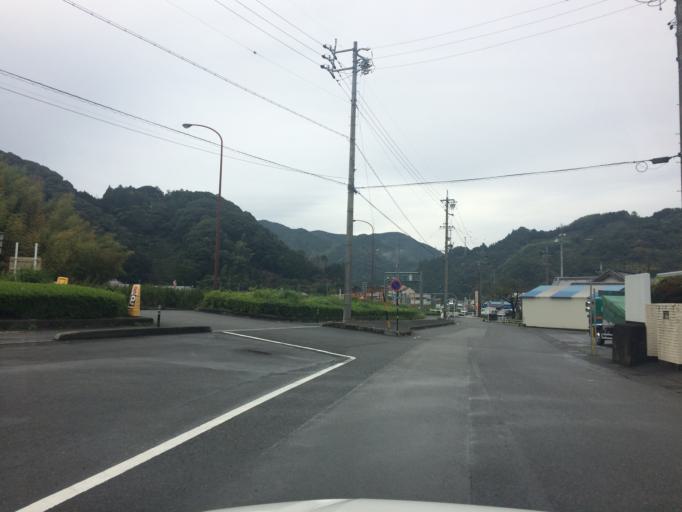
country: JP
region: Shizuoka
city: Shizuoka-shi
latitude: 34.9415
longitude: 138.3247
